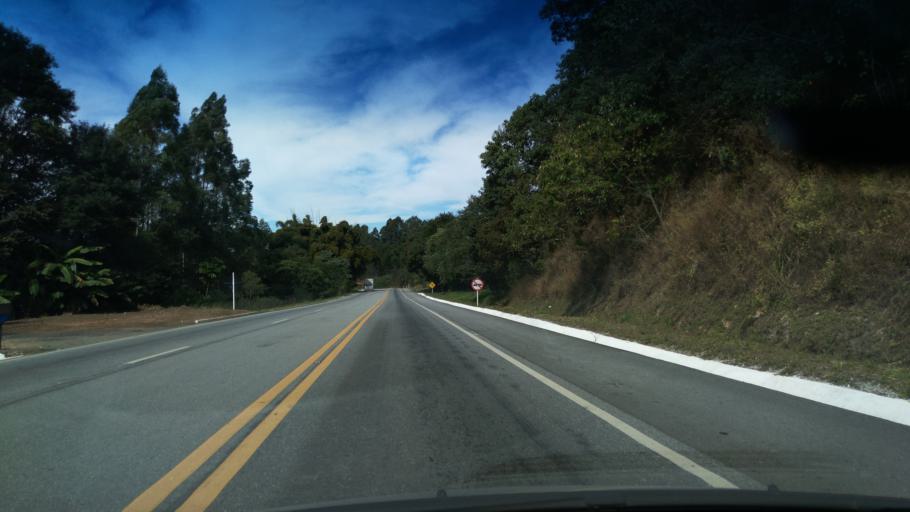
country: BR
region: Minas Gerais
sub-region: Borda Da Mata
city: Borda da Mata
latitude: -22.1366
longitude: -46.1472
